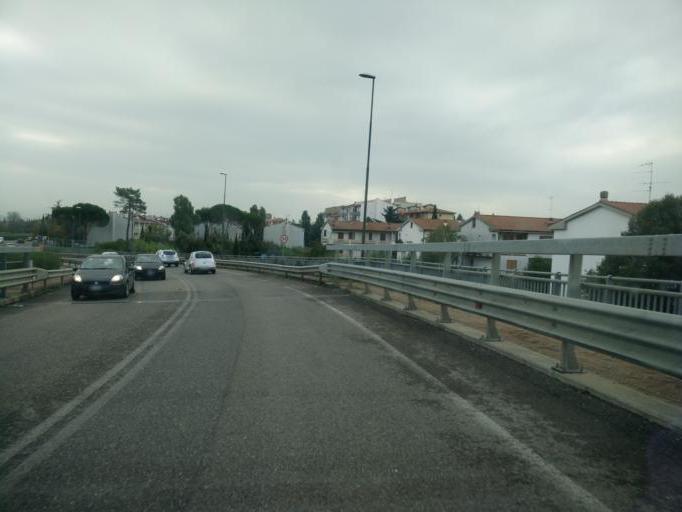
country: IT
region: Tuscany
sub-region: Province of Florence
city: Campi Bisenzio
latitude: 43.8277
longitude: 11.1392
